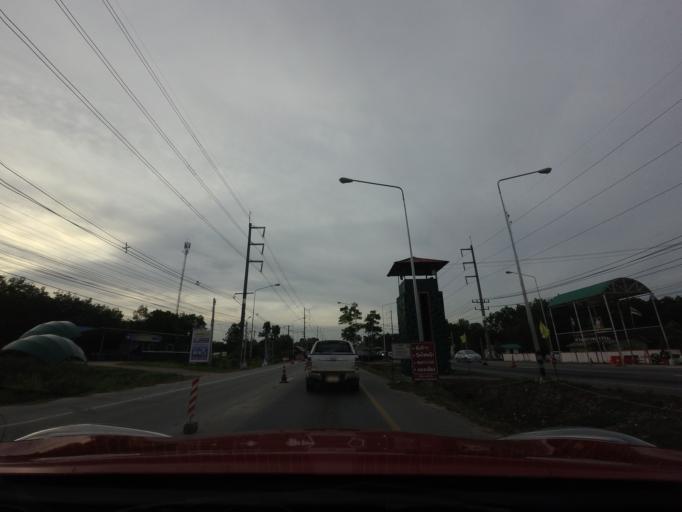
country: TH
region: Songkhla
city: Chana
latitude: 6.9579
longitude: 100.6889
